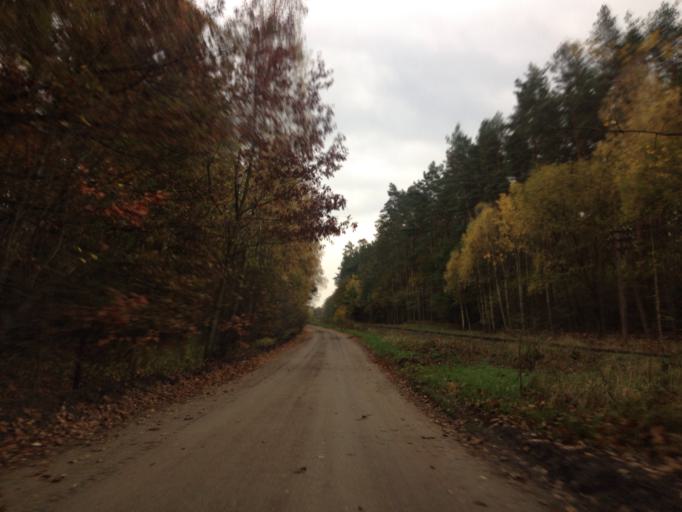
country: PL
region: Kujawsko-Pomorskie
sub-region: Powiat brodnicki
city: Bartniczka
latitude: 53.2683
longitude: 19.5770
